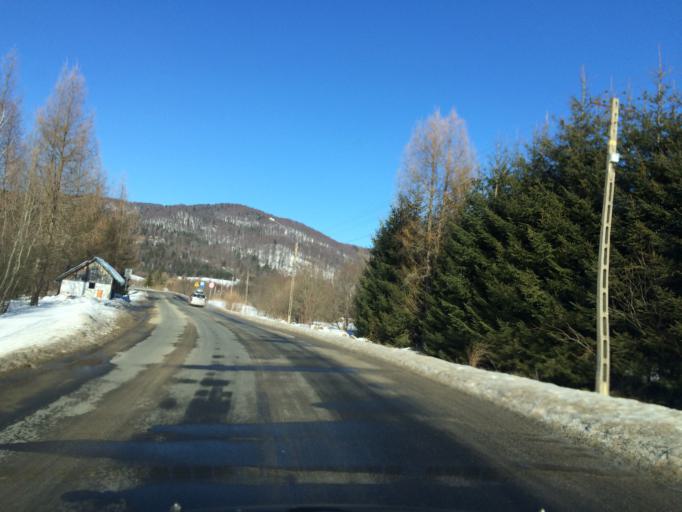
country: PL
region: Subcarpathian Voivodeship
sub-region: Powiat leski
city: Cisna
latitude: 49.1912
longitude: 22.4270
